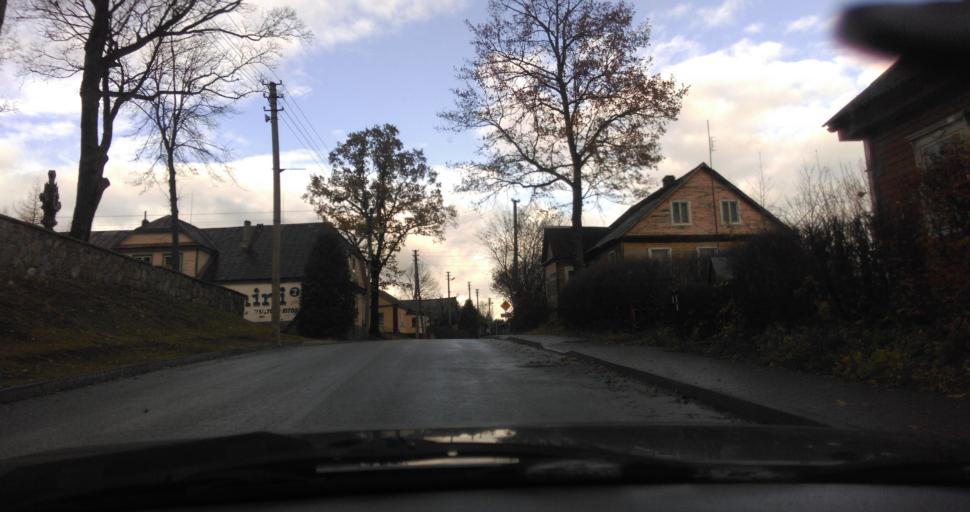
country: LT
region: Utenos apskritis
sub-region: Utena
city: Utena
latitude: 55.5854
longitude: 25.4959
